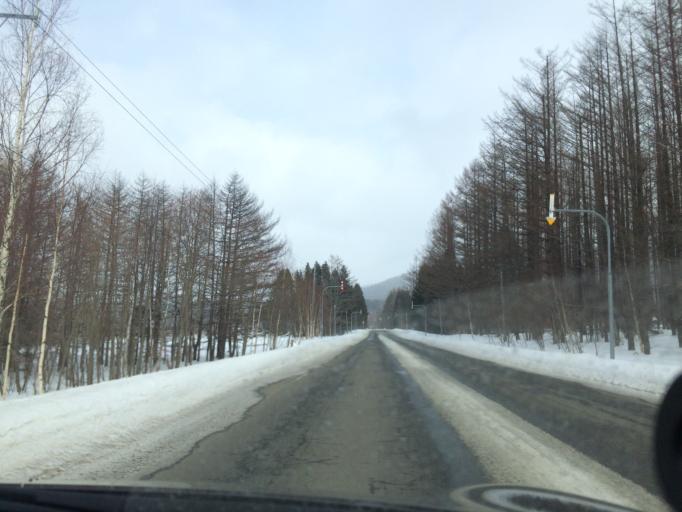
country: JP
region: Hokkaido
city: Shimo-furano
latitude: 43.0489
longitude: 142.6666
